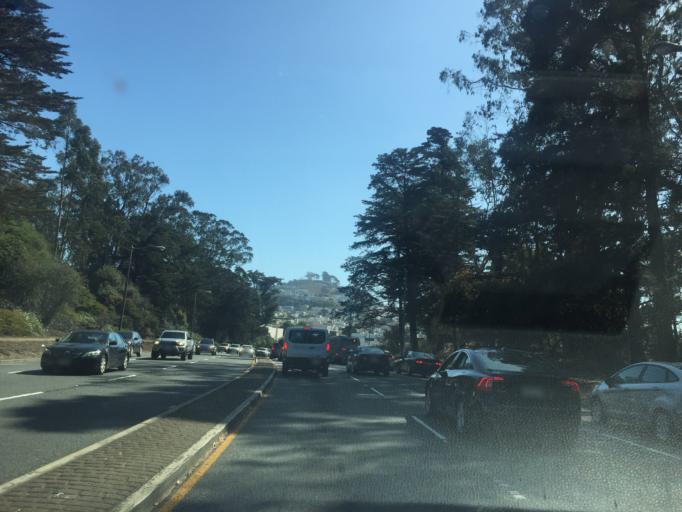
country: US
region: California
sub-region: San Francisco County
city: San Francisco
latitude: 37.7674
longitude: -122.4781
